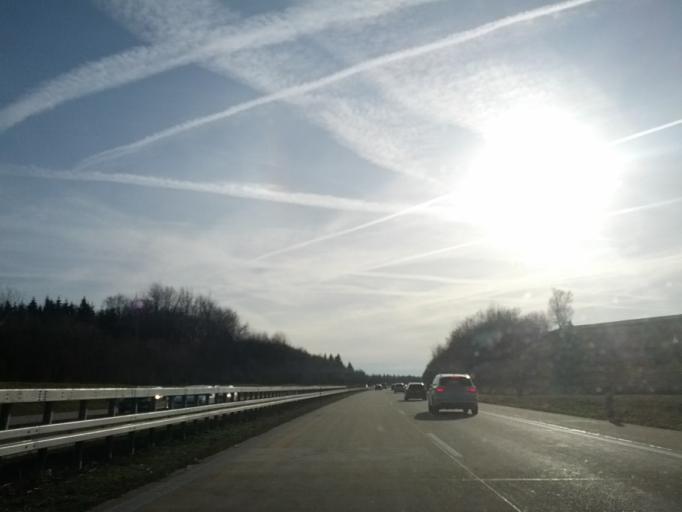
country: DE
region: Baden-Wuerttemberg
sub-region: Regierungsbezirk Stuttgart
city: Ellenberg
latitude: 48.9918
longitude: 10.1951
